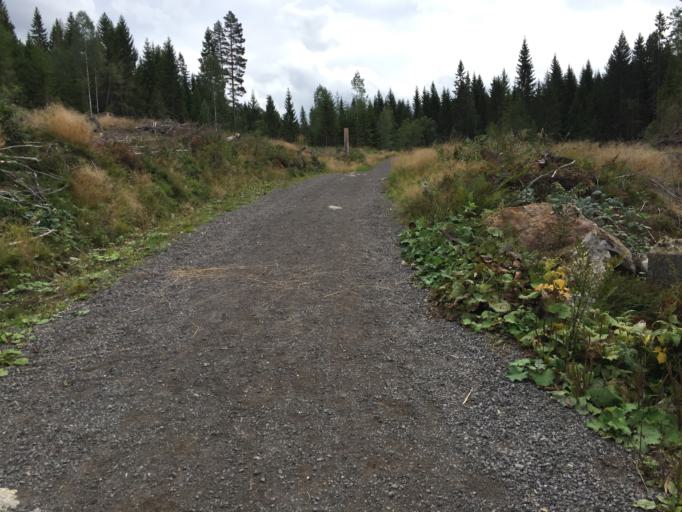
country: NO
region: Akershus
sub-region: Skedsmo
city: Lillestrom
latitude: 59.9179
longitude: 11.0135
